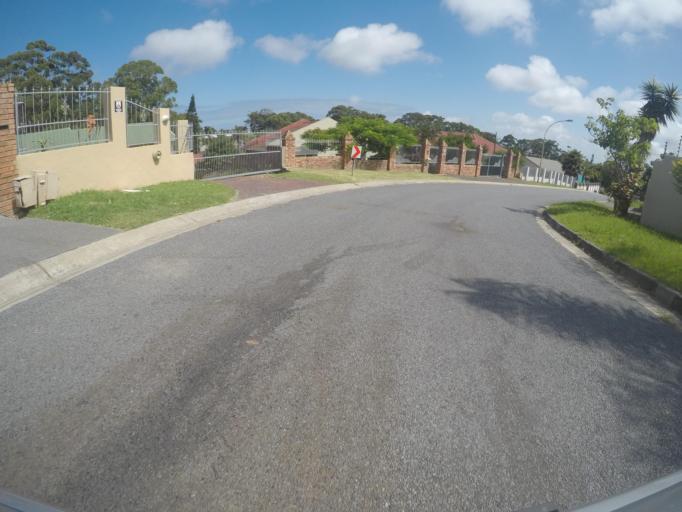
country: ZA
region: Eastern Cape
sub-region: Buffalo City Metropolitan Municipality
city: East London
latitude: -32.9987
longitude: 27.8890
